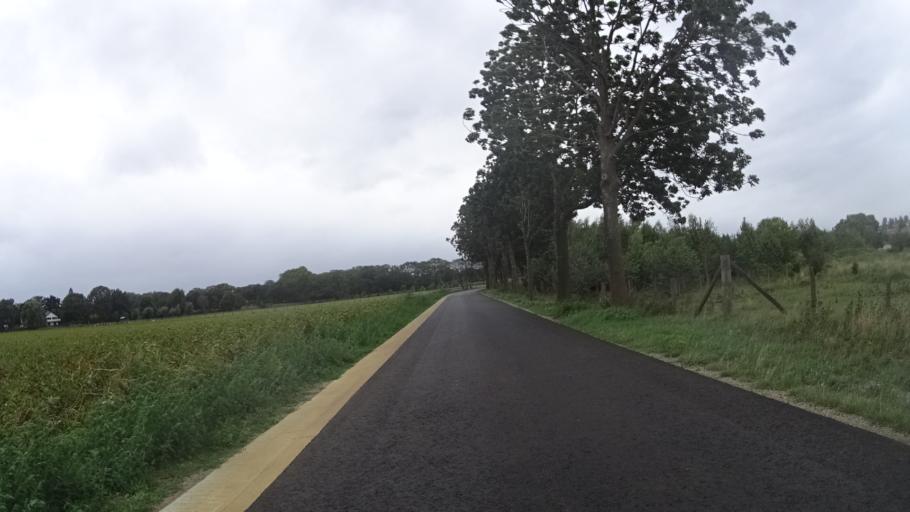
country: NL
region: Limburg
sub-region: Gemeente Venlo
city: Tegelen
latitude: 51.3370
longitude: 6.1137
